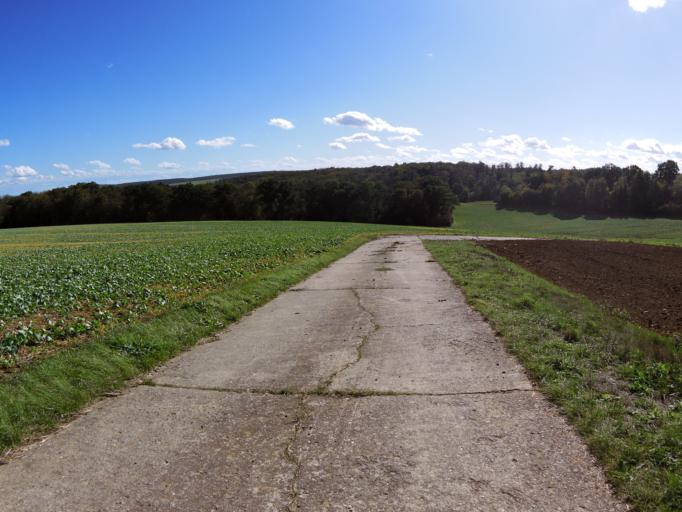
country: DE
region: Bavaria
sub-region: Regierungsbezirk Unterfranken
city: Erlabrunn
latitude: 49.8312
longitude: 9.8301
